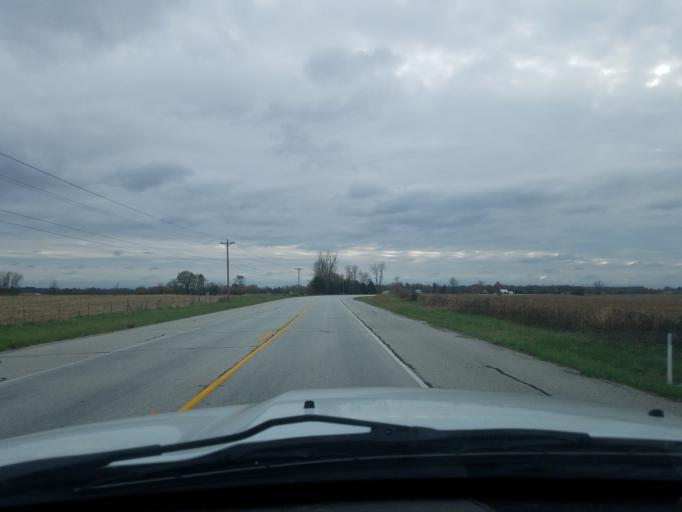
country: US
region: Indiana
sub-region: Bartholomew County
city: Hope
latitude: 39.1848
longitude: -85.7721
